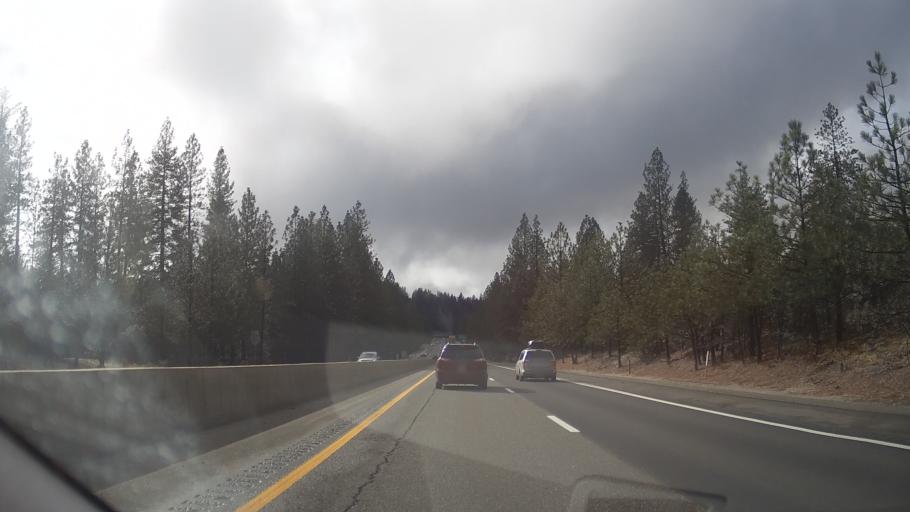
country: US
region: California
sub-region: Placer County
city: Colfax
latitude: 39.1536
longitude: -120.8904
